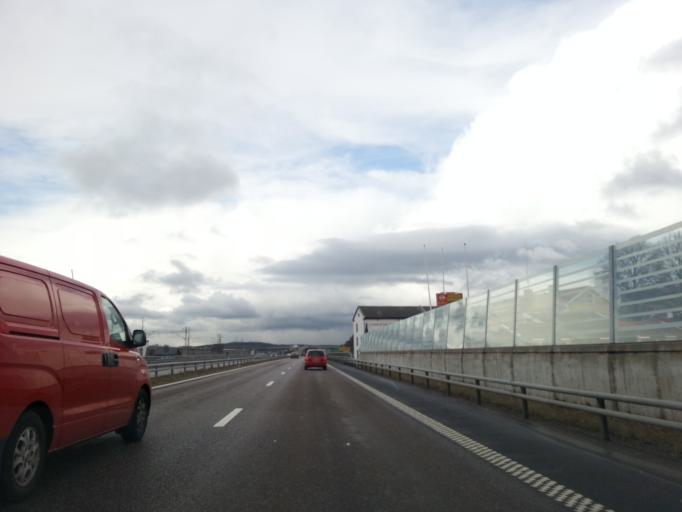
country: SE
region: Vaestra Goetaland
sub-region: Ale Kommun
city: Surte
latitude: 57.8283
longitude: 12.0136
